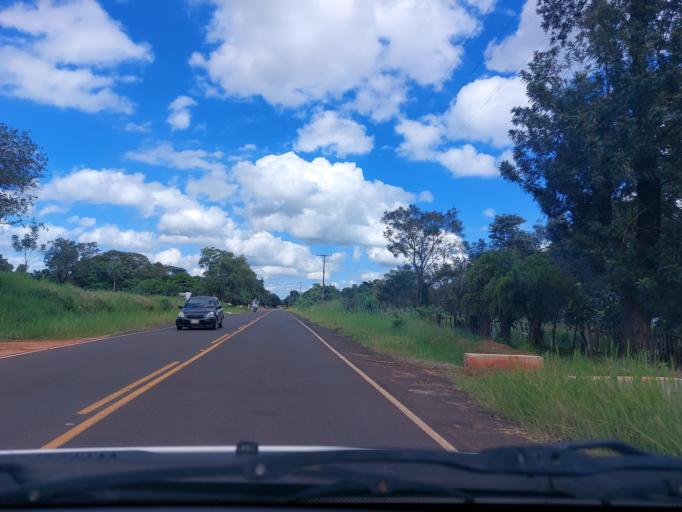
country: PY
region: San Pedro
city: Guayaybi
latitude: -24.5905
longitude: -56.5196
